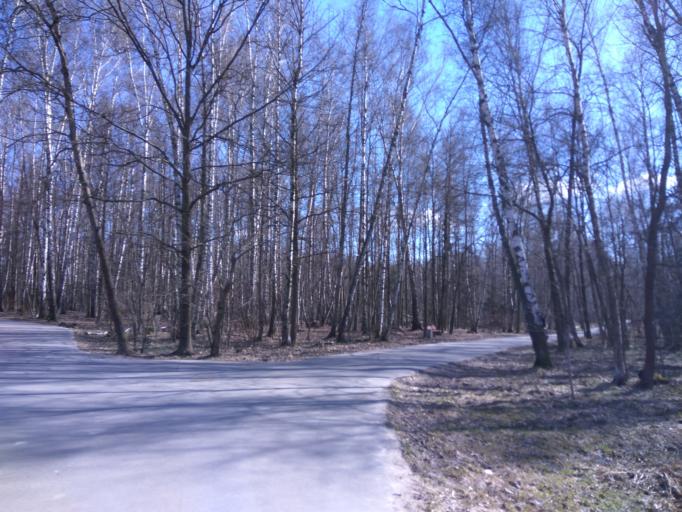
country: RU
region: Moscow
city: Ivanovskoye
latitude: 55.7860
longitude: 37.8316
